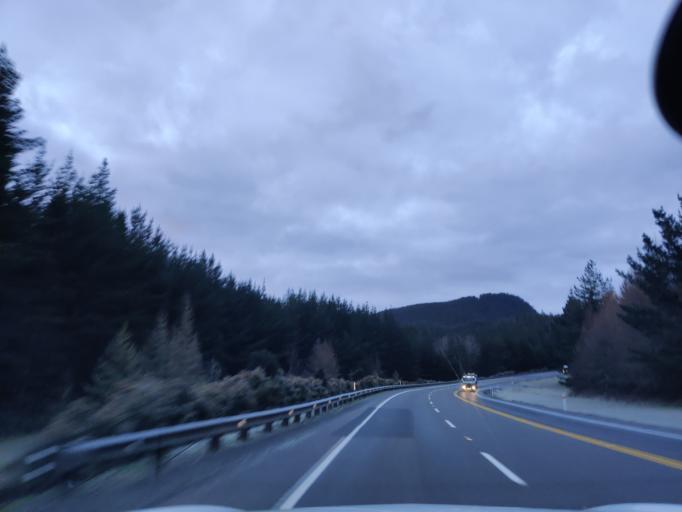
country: NZ
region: Waikato
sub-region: Taupo District
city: Taupo
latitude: -38.4326
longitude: 176.0597
